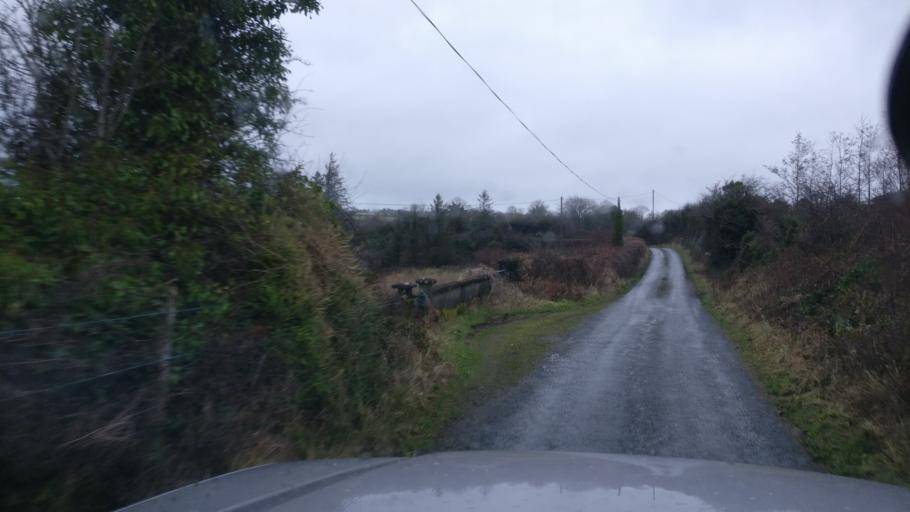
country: IE
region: Connaught
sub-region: County Galway
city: Loughrea
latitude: 53.1554
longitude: -8.6111
